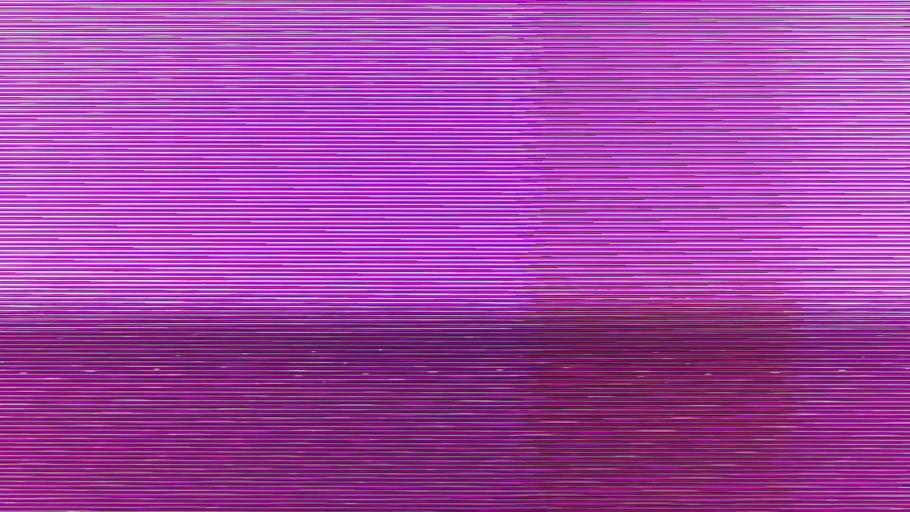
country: US
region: Wisconsin
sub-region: Racine County
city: Waterford
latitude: 42.7566
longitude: -88.2048
